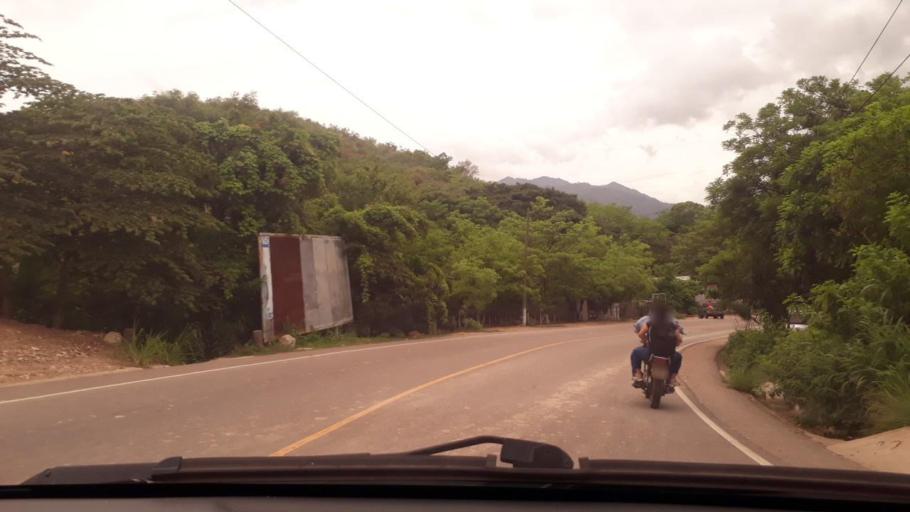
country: GT
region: Chiquimula
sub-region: Municipio de Jocotan
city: Jocotan
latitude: 14.8163
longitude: -89.3754
